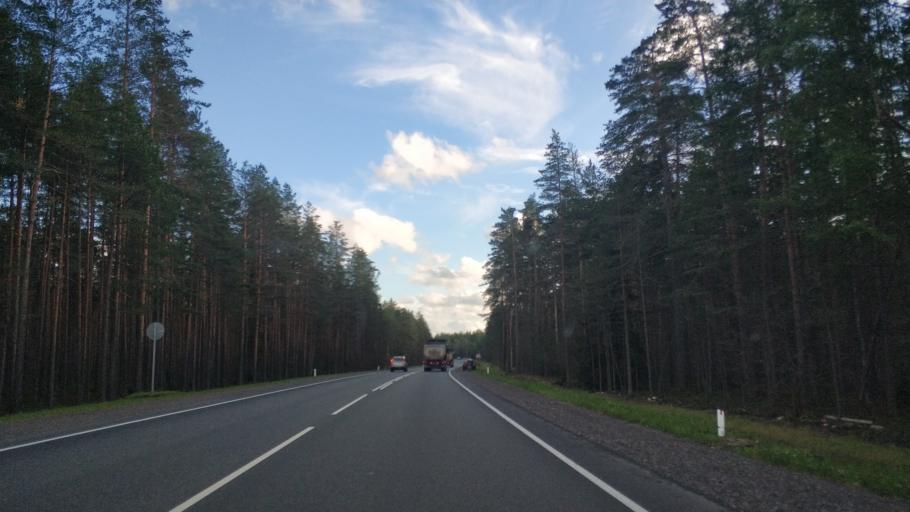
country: RU
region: Leningrad
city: Priozersk
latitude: 60.8849
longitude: 30.1608
